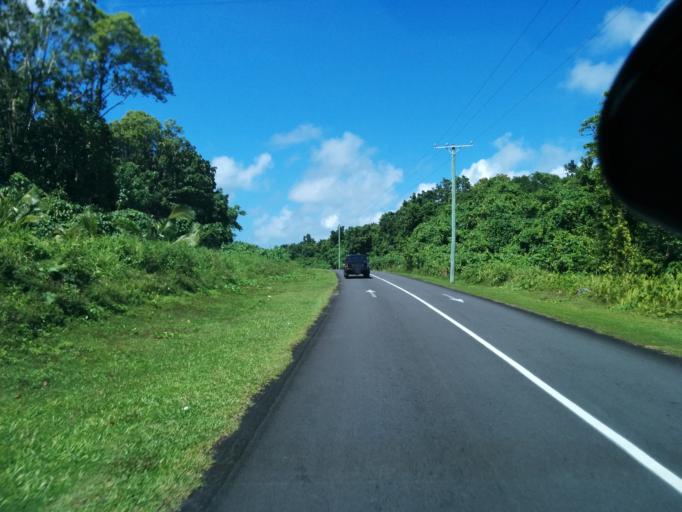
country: WS
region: Fa`asaleleaga
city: Safotulafai
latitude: -13.5532
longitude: -172.2378
